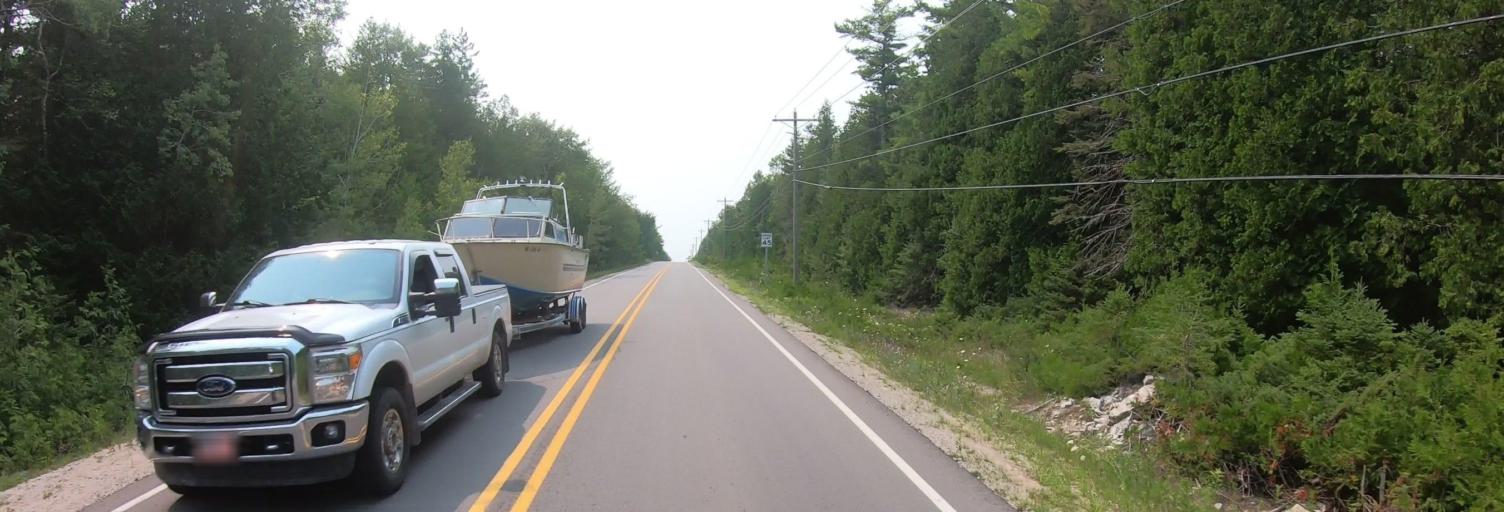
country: CA
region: Ontario
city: Thessalon
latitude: 45.9997
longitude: -83.9065
